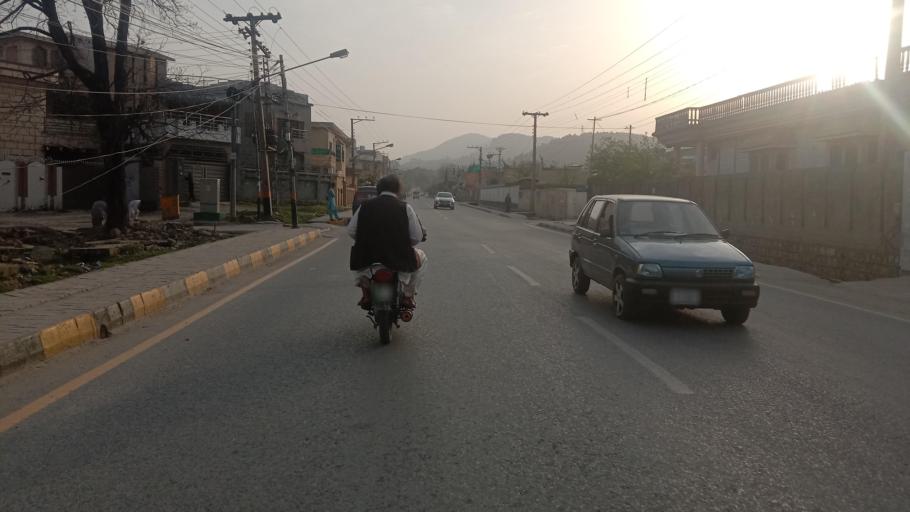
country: PK
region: Khyber Pakhtunkhwa
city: Abbottabad
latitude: 34.1699
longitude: 73.2319
